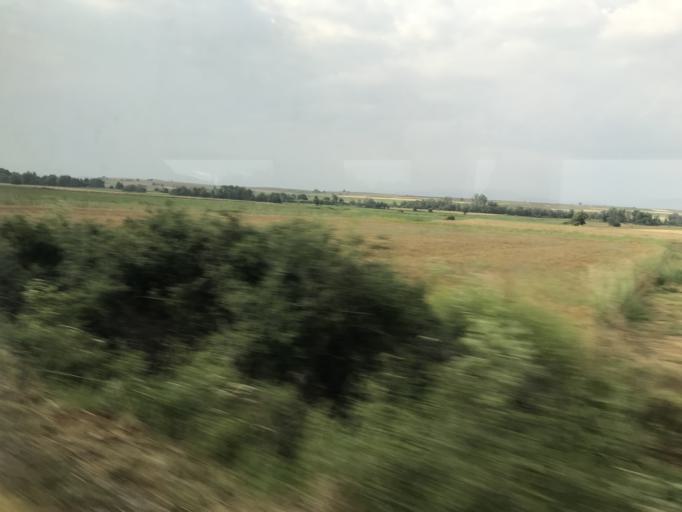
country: GR
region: East Macedonia and Thrace
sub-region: Nomos Rodopis
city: Lykeio
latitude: 41.0432
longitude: 25.6479
